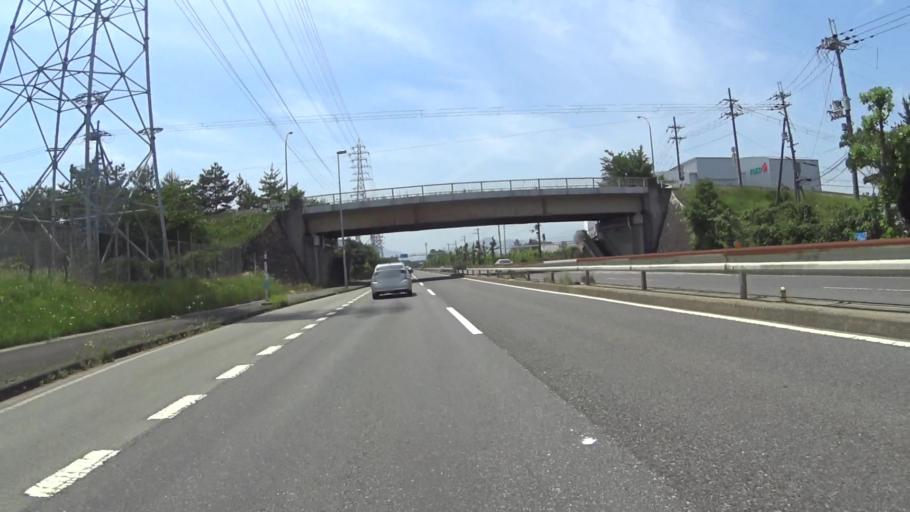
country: JP
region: Kyoto
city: Fukuchiyama
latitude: 35.2855
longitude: 135.1665
